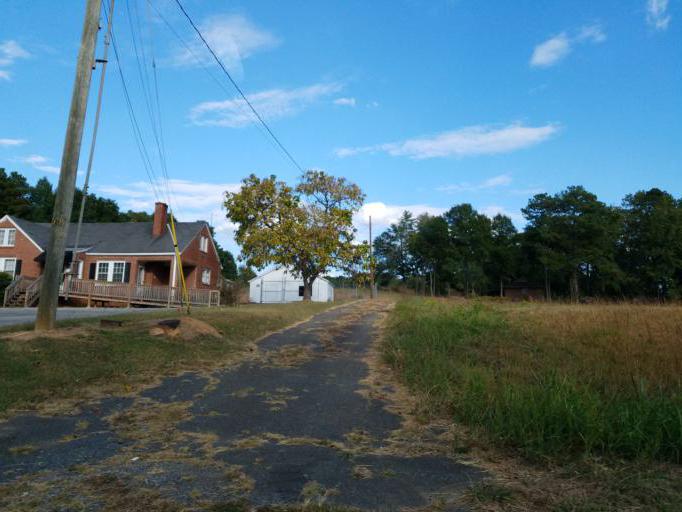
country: US
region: Georgia
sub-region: Bartow County
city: Cartersville
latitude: 34.1883
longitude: -84.7956
